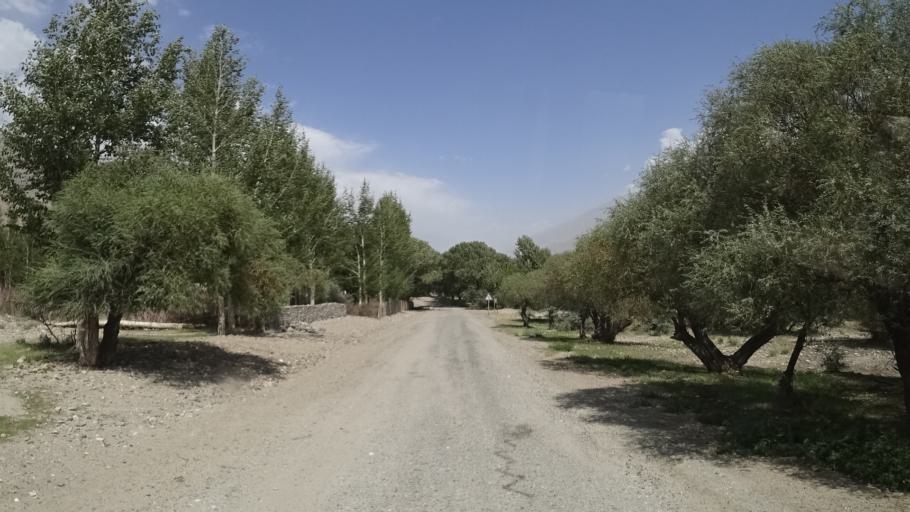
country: AF
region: Badakhshan
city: Khandud
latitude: 36.9124
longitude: 72.1804
